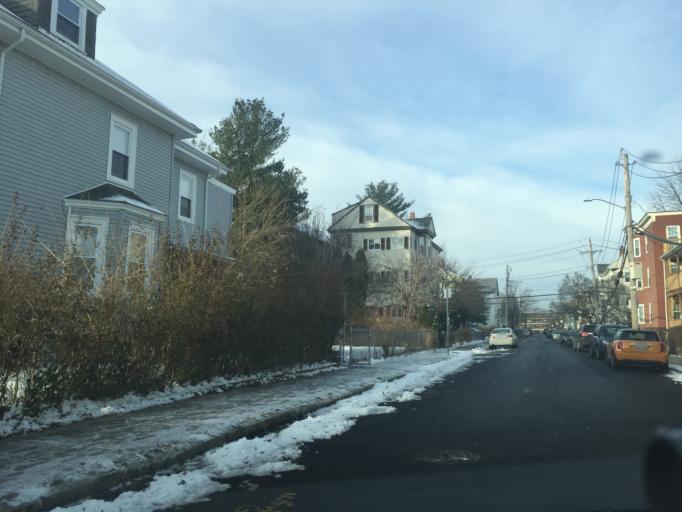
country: US
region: Massachusetts
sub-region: Norfolk County
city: Brookline
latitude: 42.3534
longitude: -71.1451
